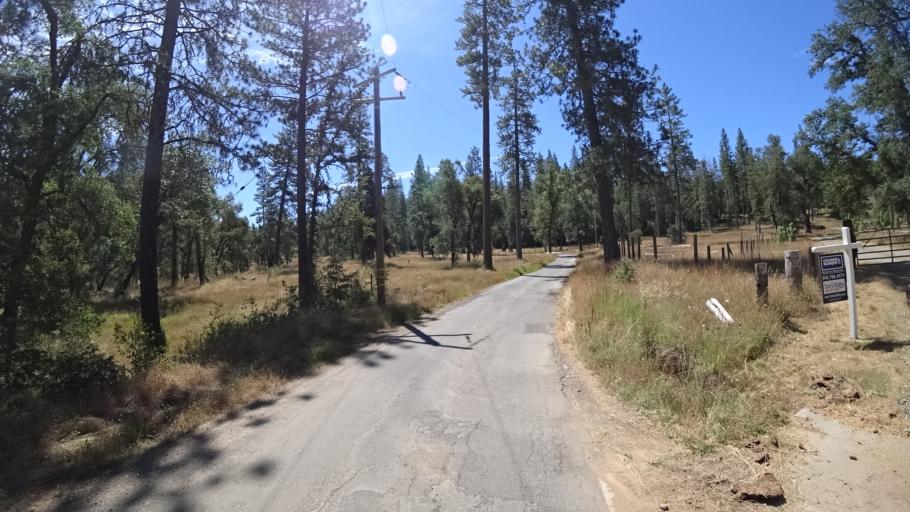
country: US
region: California
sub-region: Amador County
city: Pioneer
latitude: 38.3382
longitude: -120.5047
